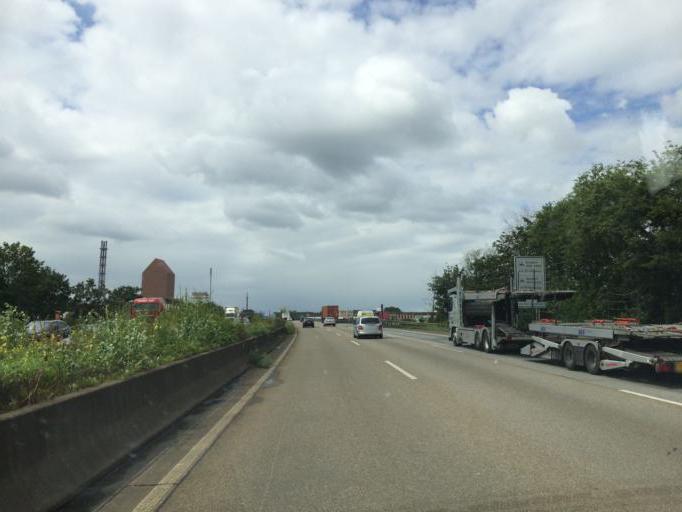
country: DE
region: North Rhine-Westphalia
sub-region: Regierungsbezirk Dusseldorf
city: Duisburg
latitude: 51.4424
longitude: 6.7636
